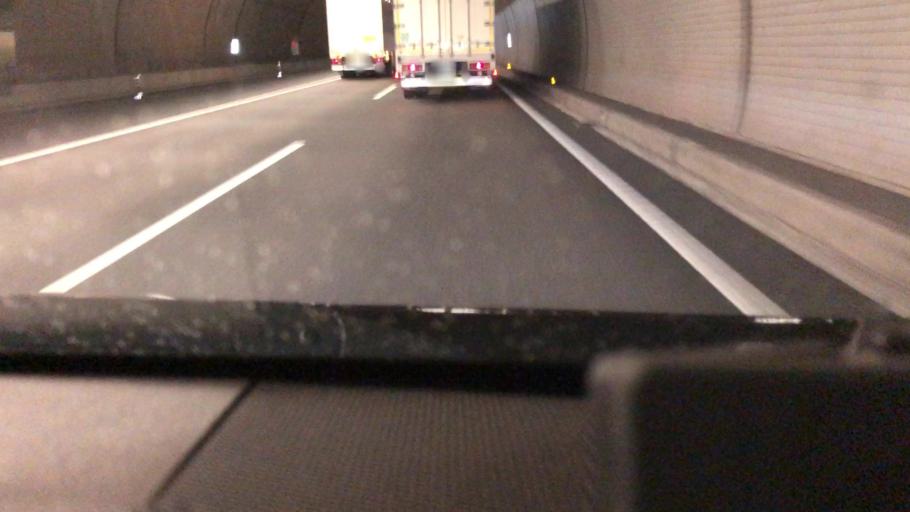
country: JP
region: Shizuoka
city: Shizuoka-shi
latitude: 35.0597
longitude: 138.4291
